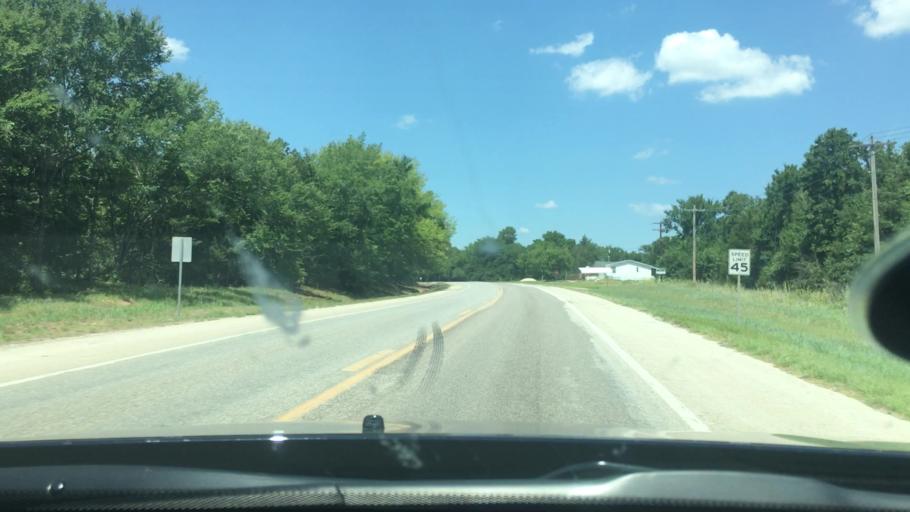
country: US
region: Oklahoma
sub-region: Carter County
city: Dickson
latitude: 34.1843
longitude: -96.8713
